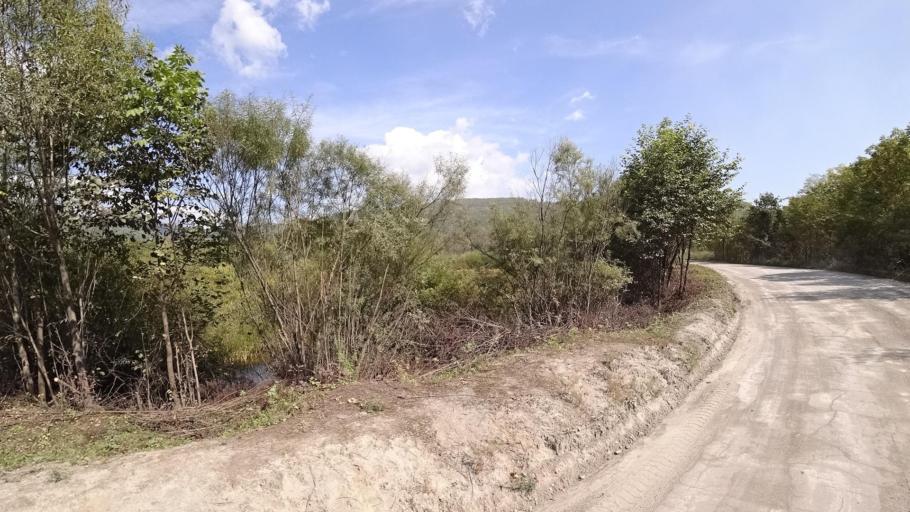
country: RU
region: Jewish Autonomous Oblast
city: Londoko
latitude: 49.0221
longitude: 131.9290
